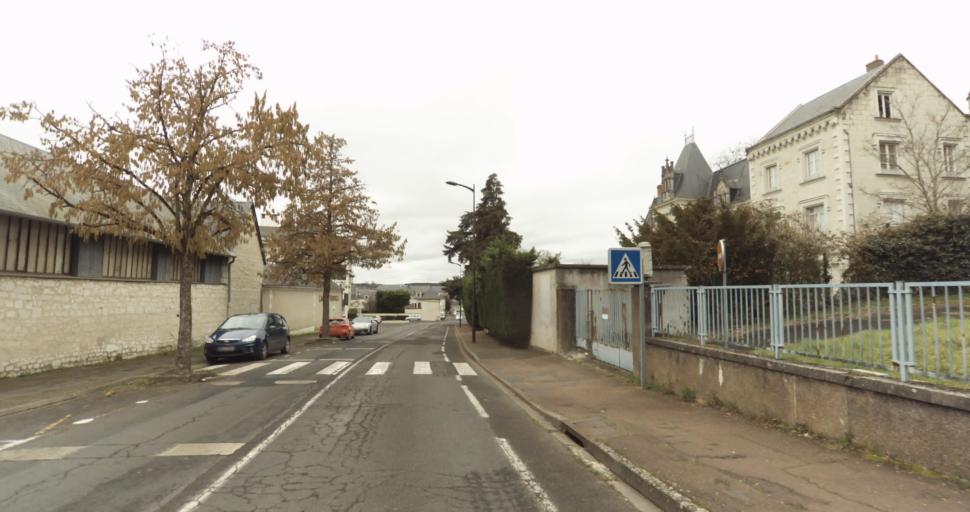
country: FR
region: Pays de la Loire
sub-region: Departement de Maine-et-Loire
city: Saumur
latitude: 47.2510
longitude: -0.0752
